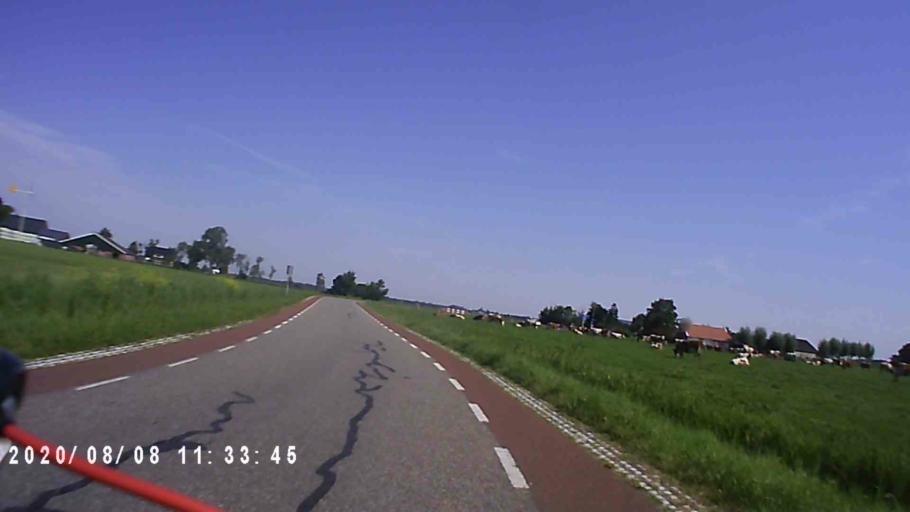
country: NL
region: Groningen
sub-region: Gemeente Zuidhorn
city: Zuidhorn
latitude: 53.2145
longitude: 6.3901
